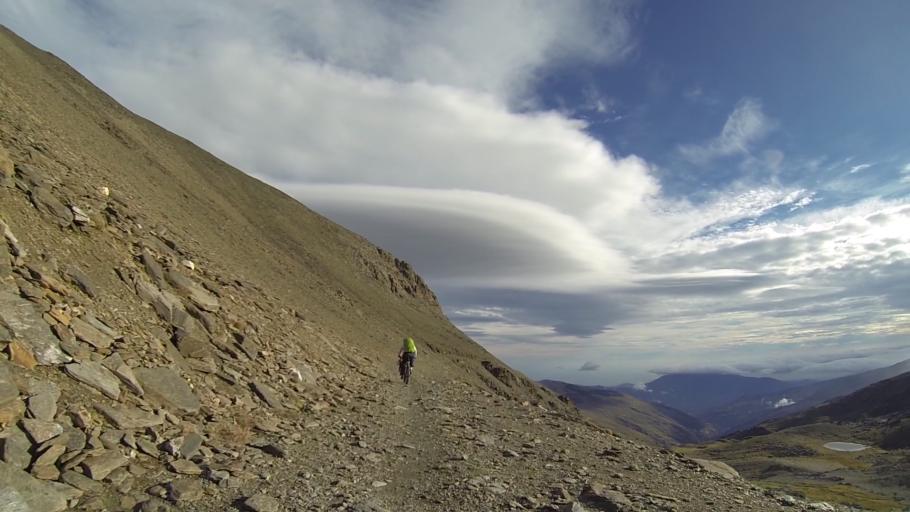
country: ES
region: Andalusia
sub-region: Provincia de Granada
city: Trevelez
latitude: 37.0508
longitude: -3.3212
